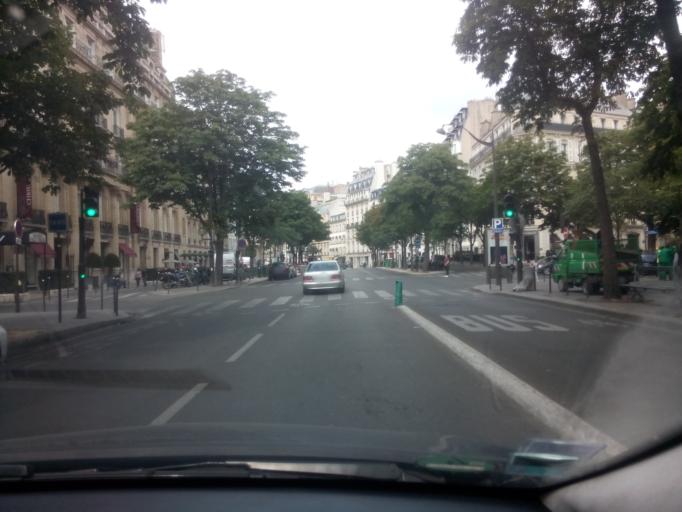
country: FR
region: Ile-de-France
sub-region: Departement des Hauts-de-Seine
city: Clichy
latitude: 48.8697
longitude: 2.3115
